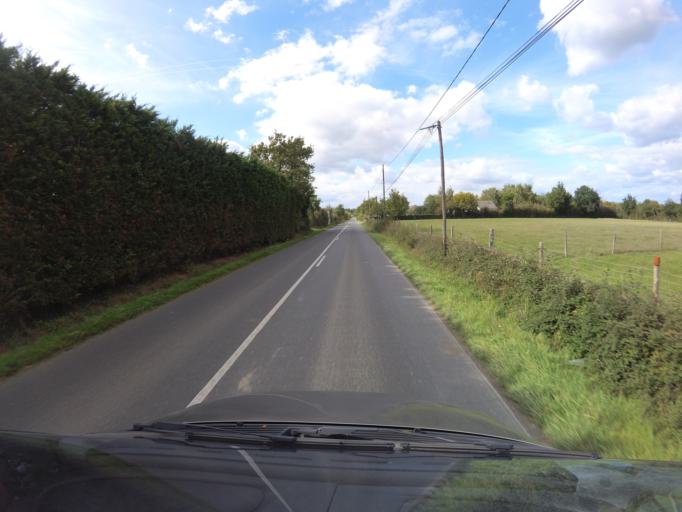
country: FR
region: Pays de la Loire
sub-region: Departement de la Loire-Atlantique
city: Casson
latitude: 47.3994
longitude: -1.5720
